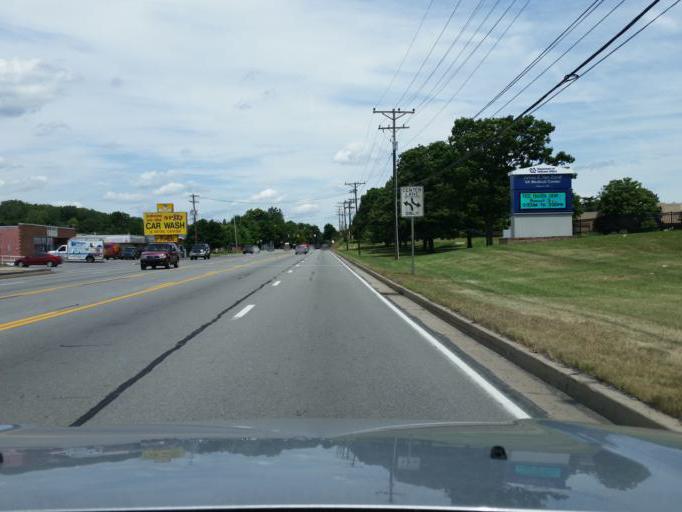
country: US
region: Pennsylvania
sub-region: Blair County
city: Lakemont
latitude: 40.4890
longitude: -78.3983
